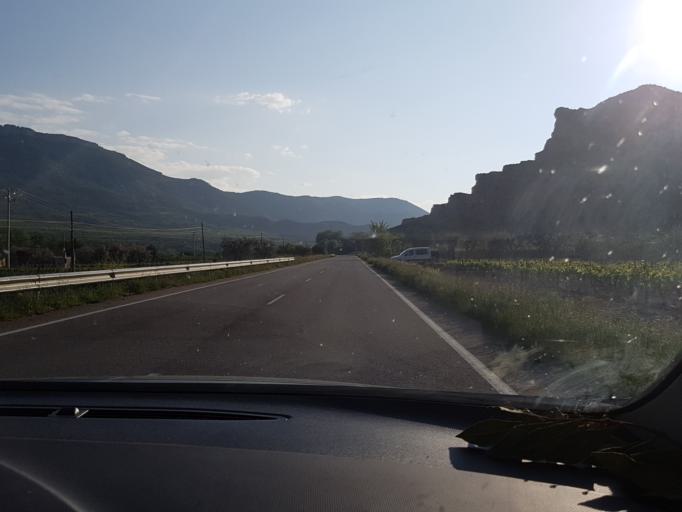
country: ES
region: La Rioja
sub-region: Provincia de La Rioja
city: Herce
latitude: 42.2134
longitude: -2.1695
